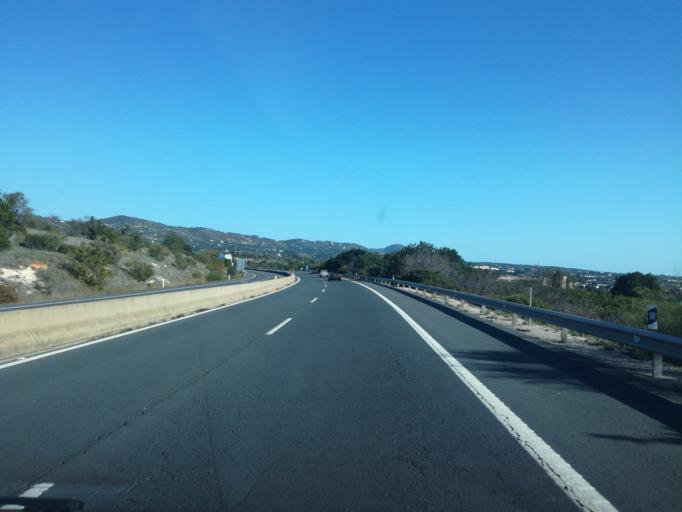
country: PT
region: Faro
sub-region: Faro
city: Santa Barbara de Nexe
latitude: 37.0925
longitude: -7.9234
